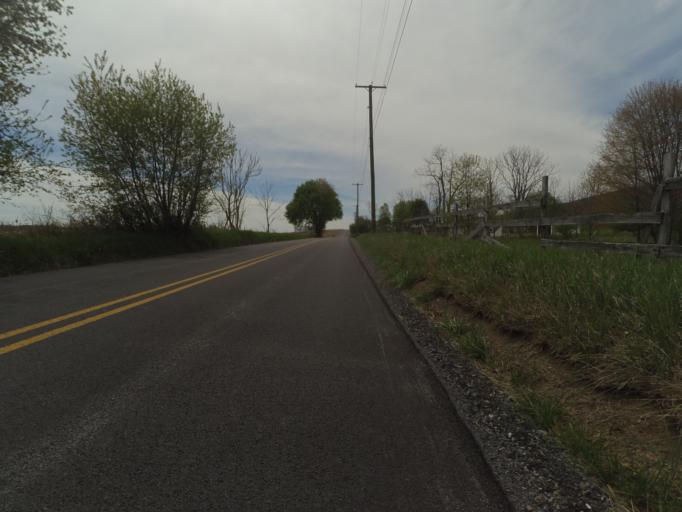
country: US
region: Pennsylvania
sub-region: Blair County
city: Tyrone
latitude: 40.6890
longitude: -78.1919
